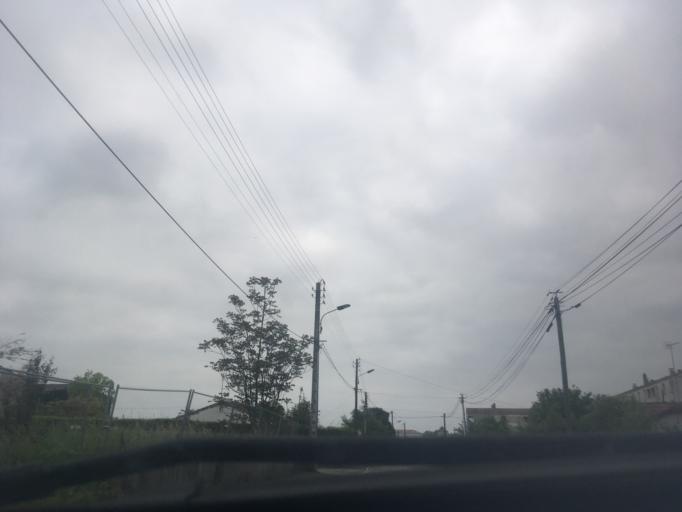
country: FR
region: Poitou-Charentes
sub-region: Departement de la Charente
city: Chateaubernard
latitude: 45.6823
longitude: -0.3346
